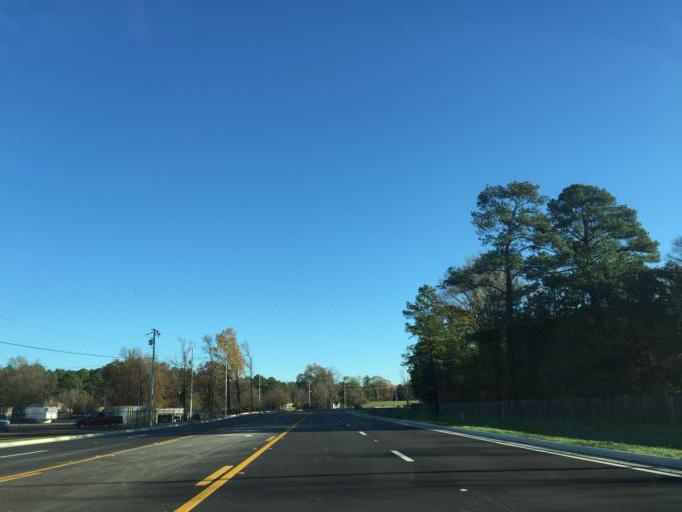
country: US
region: Mississippi
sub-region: Rankin County
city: Flowood
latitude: 32.3158
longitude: -90.1360
